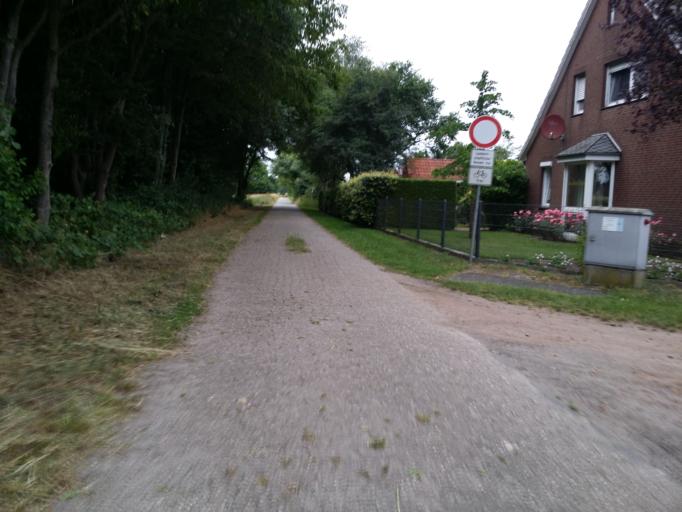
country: DE
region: Lower Saxony
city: Stuhr
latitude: 53.0007
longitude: 8.7624
